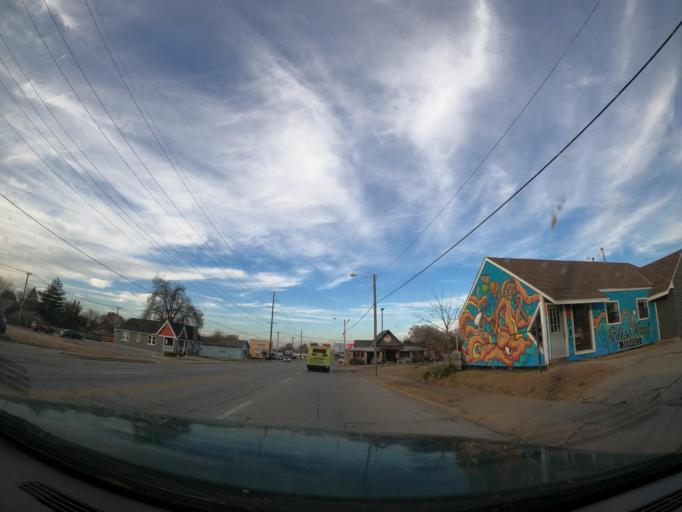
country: US
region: Oklahoma
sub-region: Tulsa County
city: Tulsa
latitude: 36.1379
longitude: -95.9403
